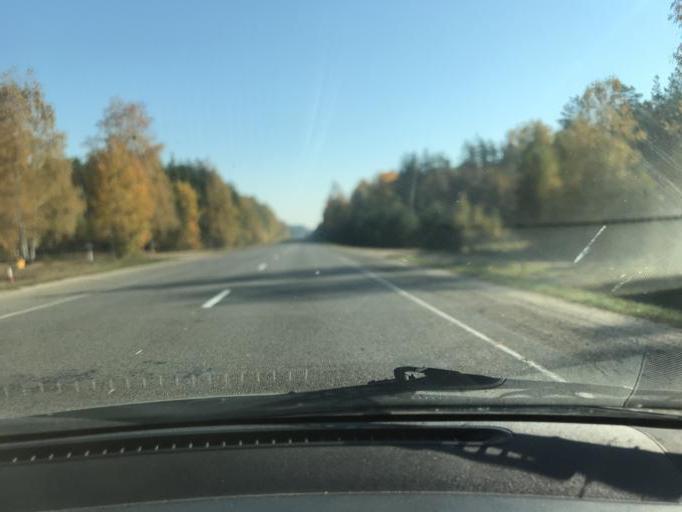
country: BY
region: Brest
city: Luninyets
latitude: 52.2698
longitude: 26.9976
